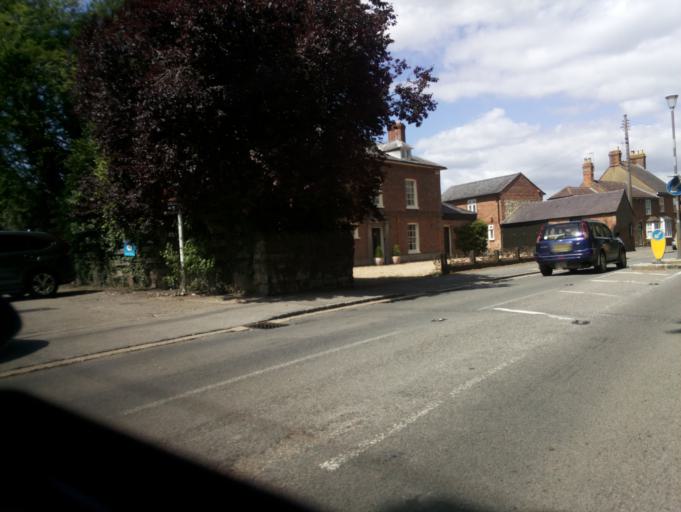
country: GB
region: England
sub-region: Buckinghamshire
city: Aylesbury
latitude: 51.8777
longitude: -0.8338
